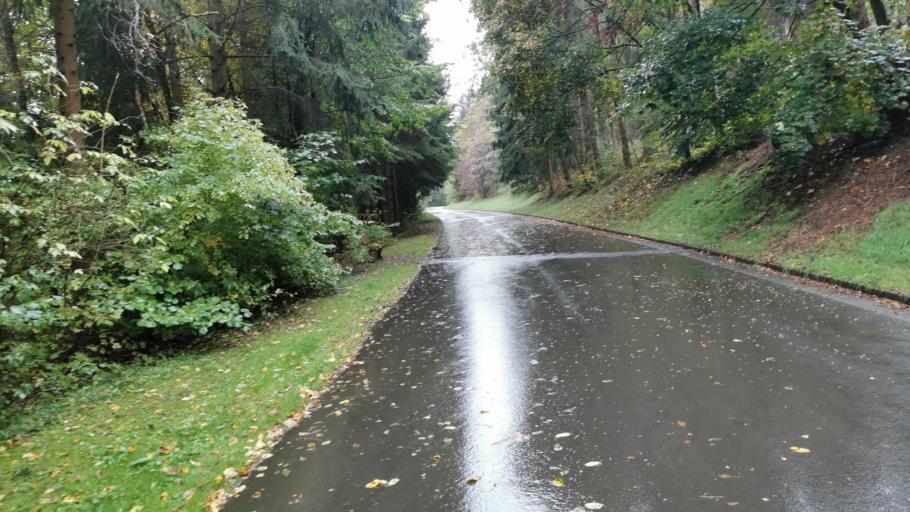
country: DE
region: Bavaria
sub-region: Upper Franconia
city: Steinwiesen
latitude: 50.3247
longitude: 11.4918
